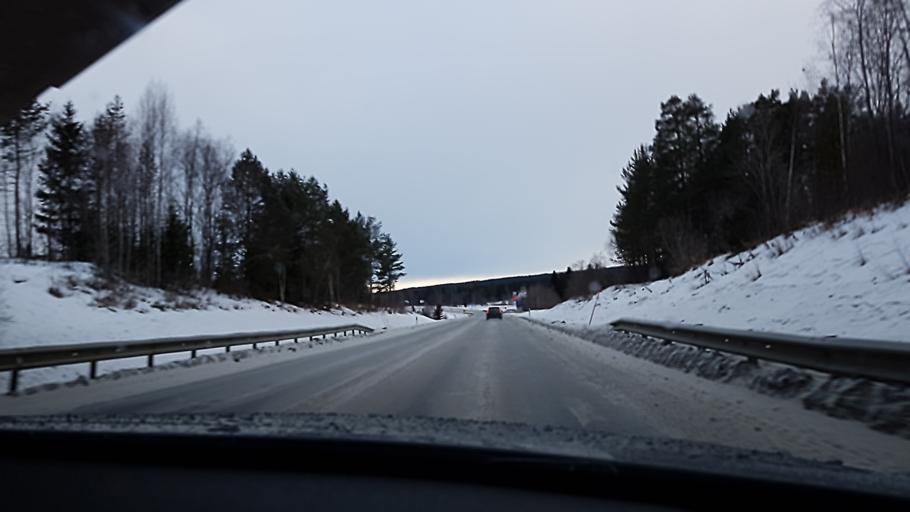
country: SE
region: Jaemtland
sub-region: Bergs Kommun
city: Hoverberg
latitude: 62.7551
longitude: 14.4338
